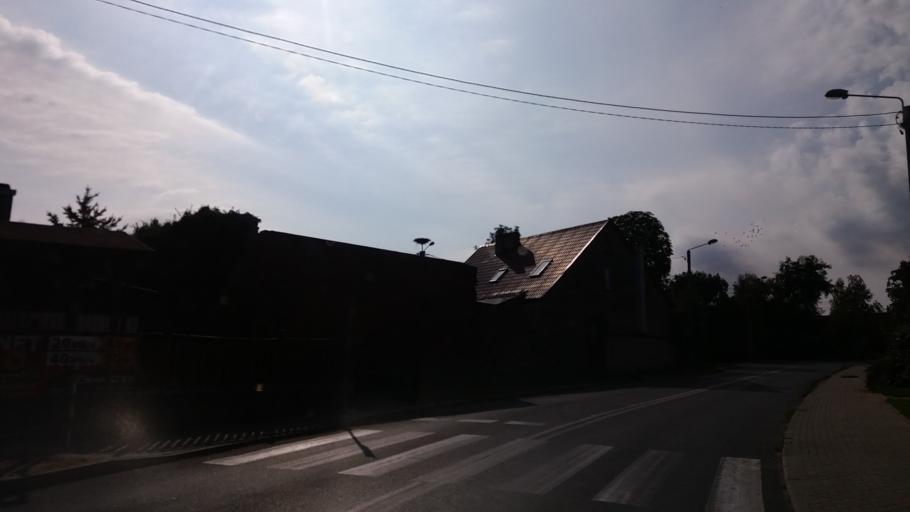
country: PL
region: West Pomeranian Voivodeship
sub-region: Powiat stargardzki
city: Suchan
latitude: 53.2268
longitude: 15.3008
